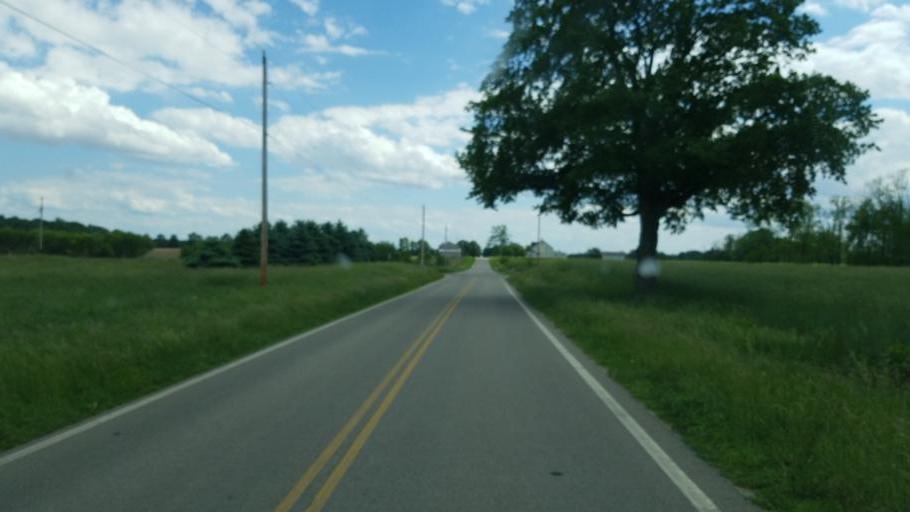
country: US
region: Ohio
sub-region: Huron County
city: Plymouth
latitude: 41.0792
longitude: -82.6108
